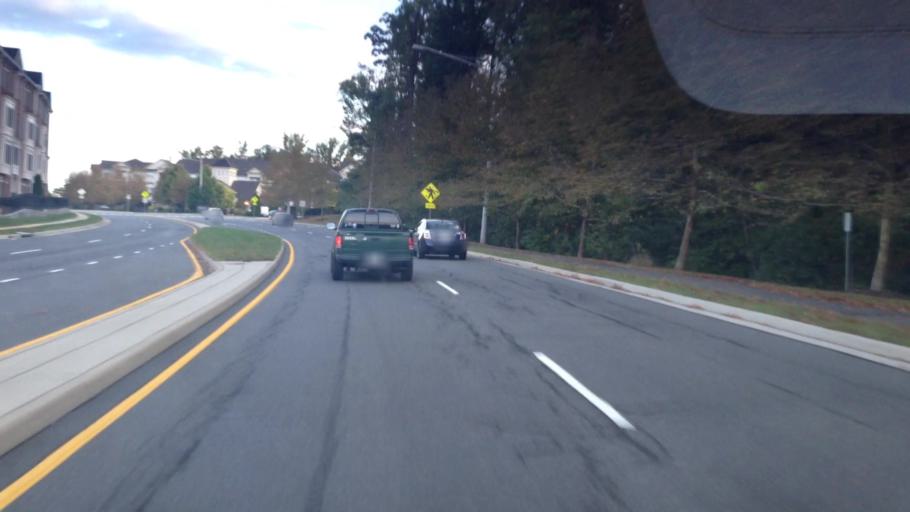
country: US
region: Virginia
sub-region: Fairfax County
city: Greenbriar
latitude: 38.8512
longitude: -77.3648
